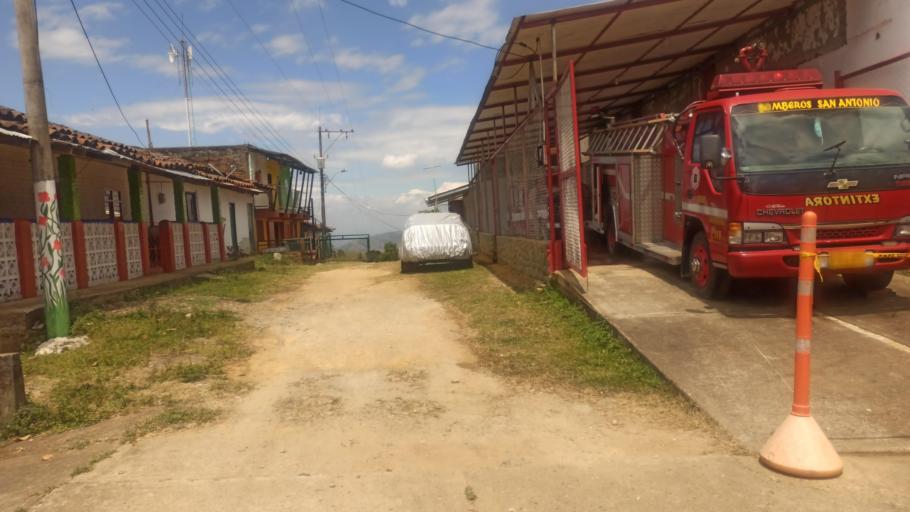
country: CO
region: Valle del Cauca
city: Jamundi
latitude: 3.2093
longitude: -76.6532
